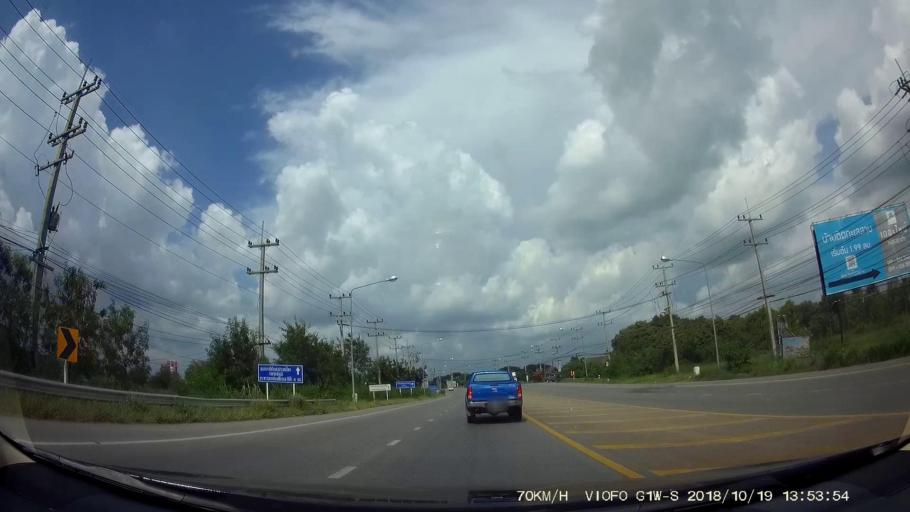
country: TH
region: Chaiyaphum
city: Chaiyaphum
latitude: 15.7818
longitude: 102.0262
